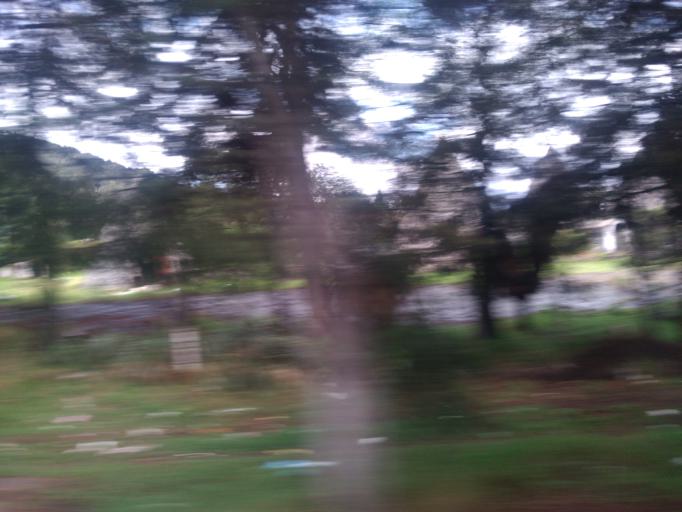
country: MX
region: Tlaxcala
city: Atexcatzingo
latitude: 19.4515
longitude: -98.1262
